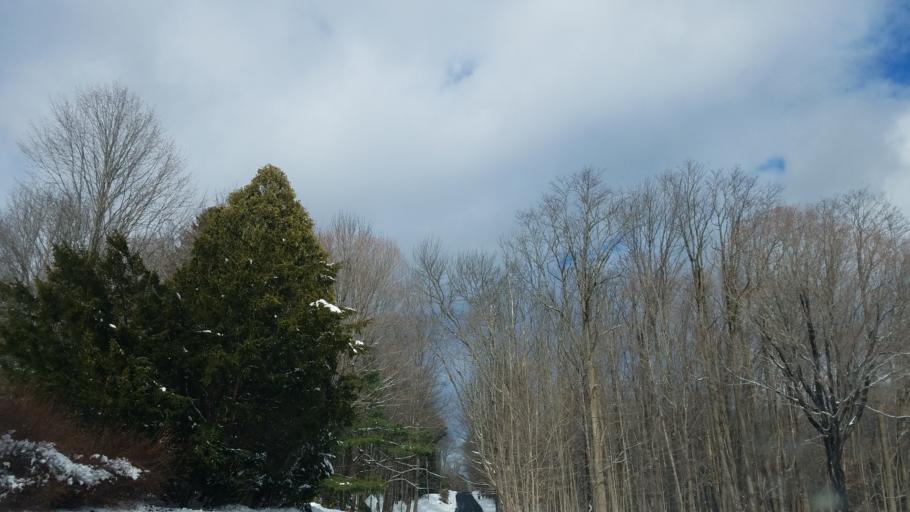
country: US
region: Connecticut
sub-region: Litchfield County
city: Winsted
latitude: 41.9665
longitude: -73.0750
